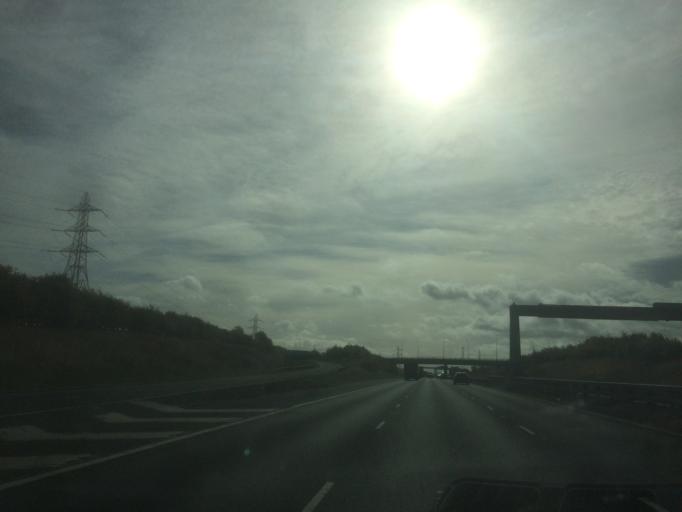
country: GB
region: England
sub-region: City and Borough of Leeds
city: Ledsham
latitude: 53.7661
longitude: -1.2845
